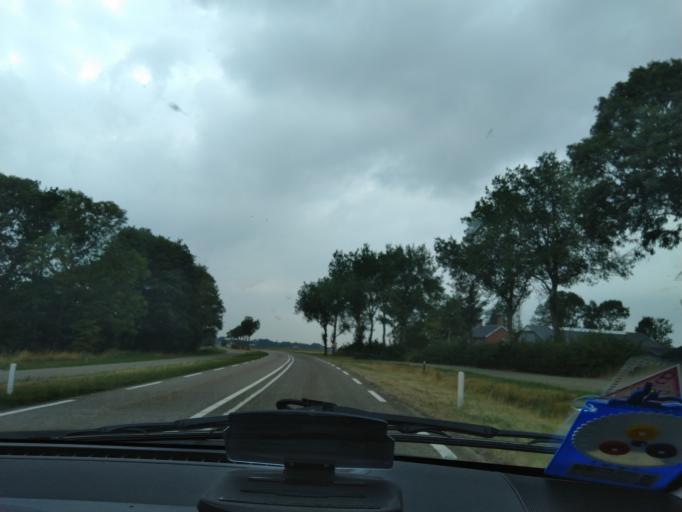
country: NL
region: Groningen
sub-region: Gemeente Vlagtwedde
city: Vlagtwedde
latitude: 53.1080
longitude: 7.1165
